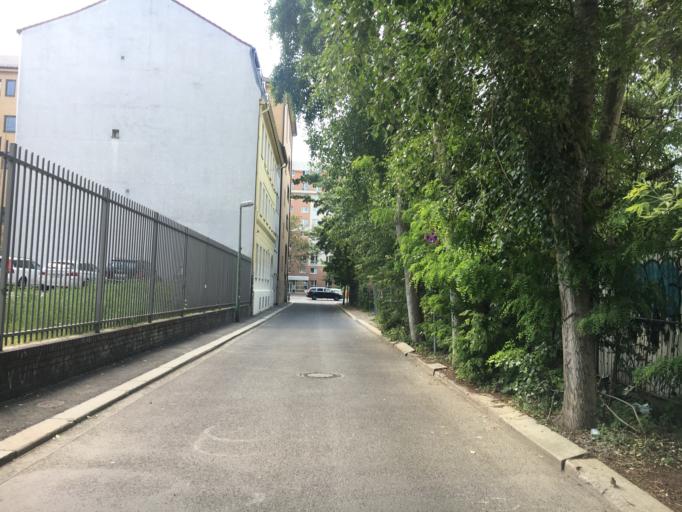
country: DE
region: Berlin
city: Berlin
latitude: 52.5115
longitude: 13.4180
